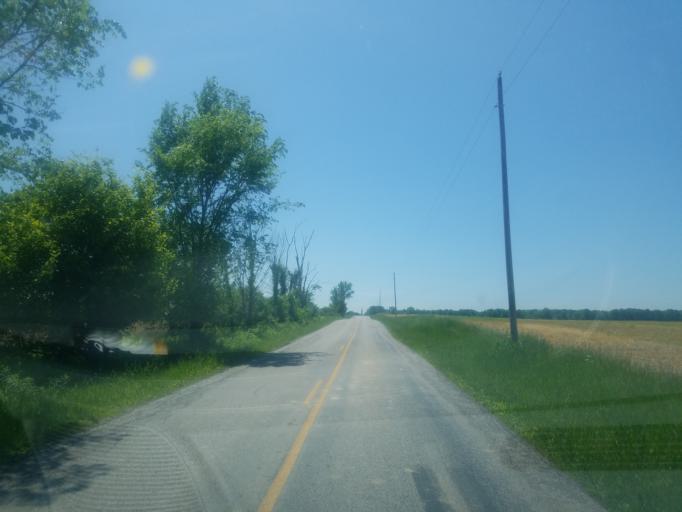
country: US
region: Ohio
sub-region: Huron County
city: New London
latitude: 41.1422
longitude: -82.3793
